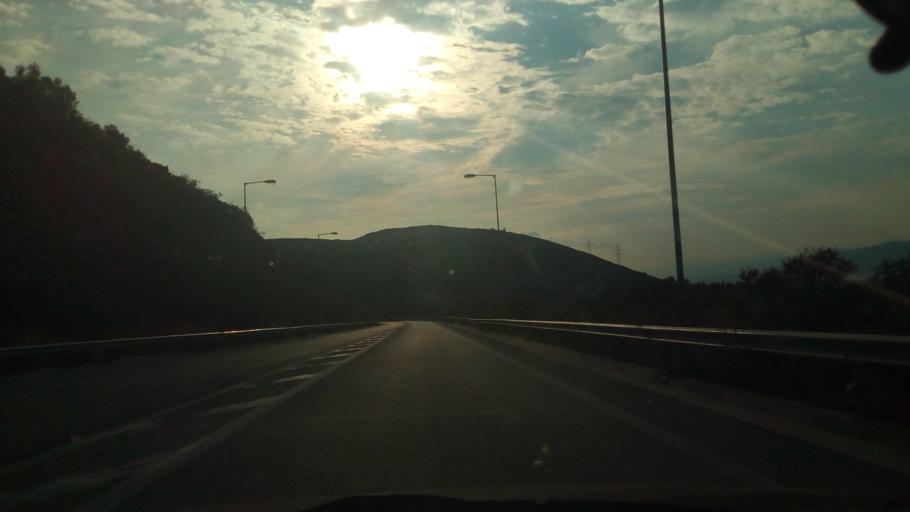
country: GR
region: West Greece
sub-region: Nomos Aitolias kai Akarnanias
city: Nafpaktos
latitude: 38.4130
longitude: 21.8455
